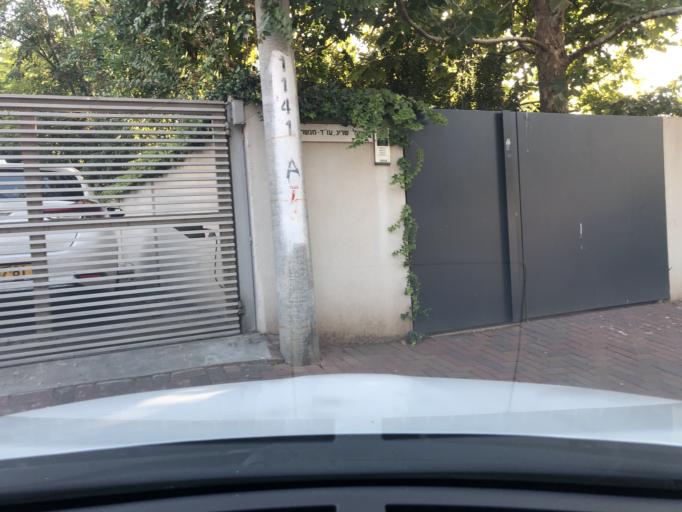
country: IL
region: Central District
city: Hod HaSharon
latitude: 32.1423
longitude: 34.9005
